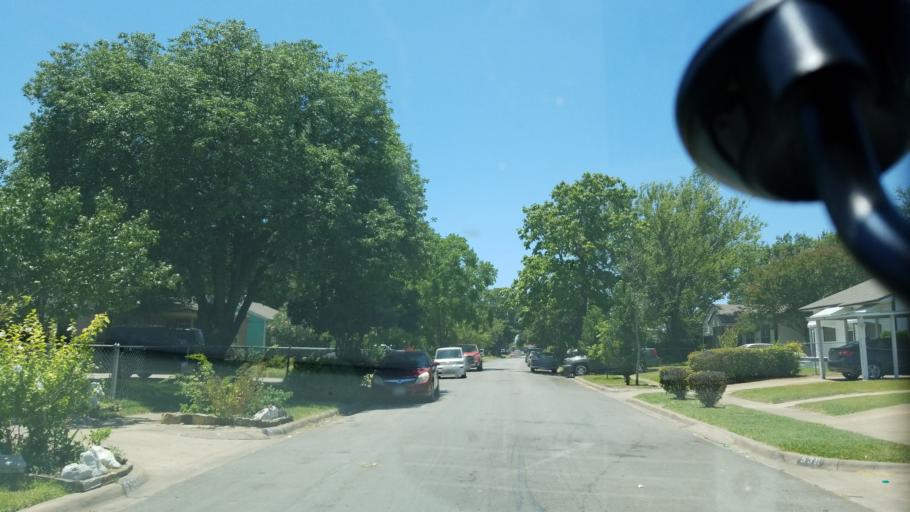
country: US
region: Texas
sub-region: Dallas County
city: Cockrell Hill
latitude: 32.7093
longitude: -96.8327
